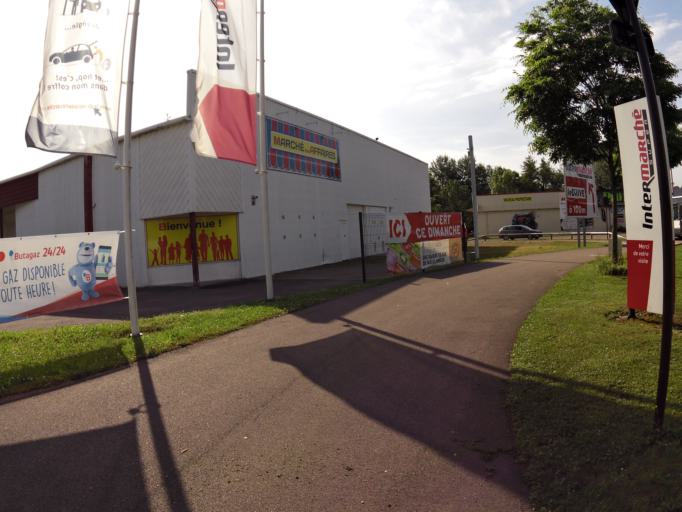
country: FR
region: Champagne-Ardenne
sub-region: Departement de l'Aube
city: Saint-Julien-les-Villas
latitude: 48.2806
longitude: 4.0955
